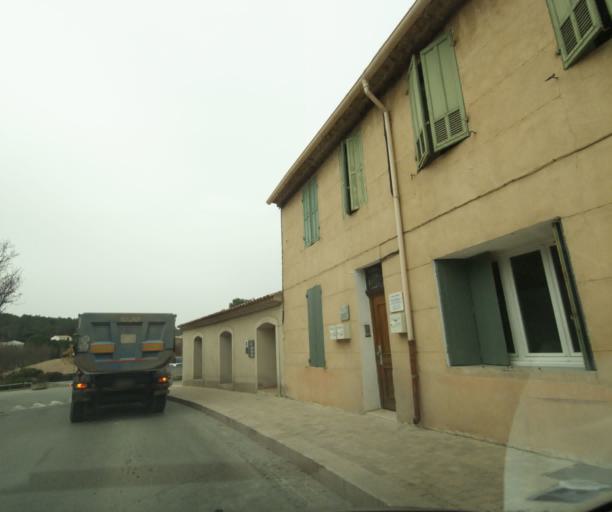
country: FR
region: Provence-Alpes-Cote d'Azur
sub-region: Departement des Bouches-du-Rhone
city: Peynier
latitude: 43.4466
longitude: 5.6377
